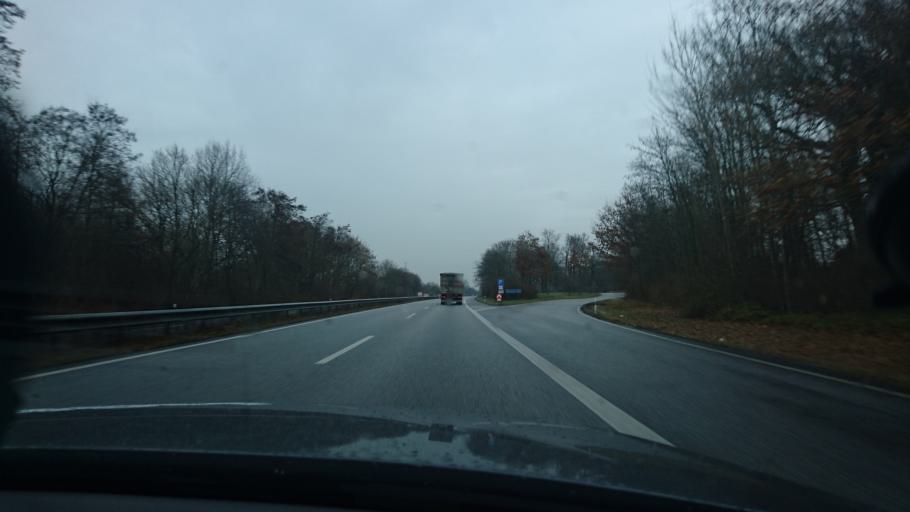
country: DE
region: Schleswig-Holstein
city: Altenkrempe
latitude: 54.1512
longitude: 10.8510
